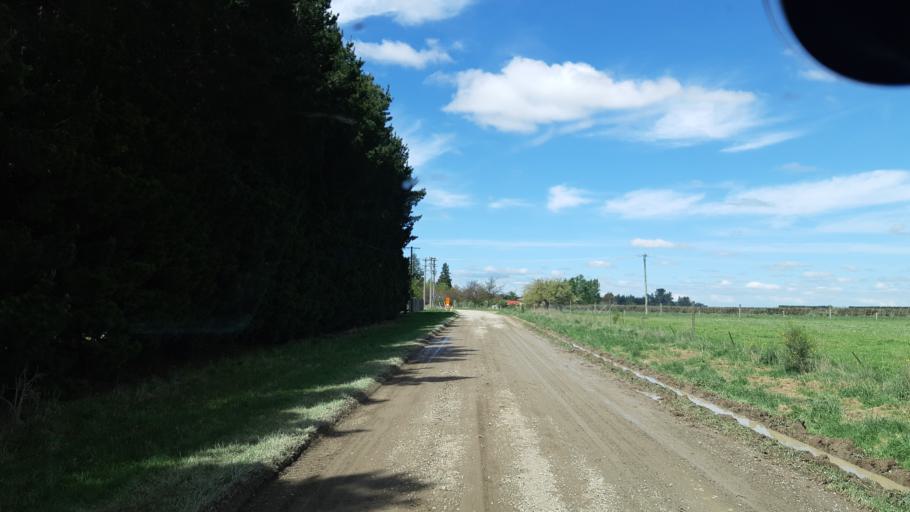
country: NZ
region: Canterbury
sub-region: Ashburton District
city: Methven
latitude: -43.6929
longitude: 171.4561
